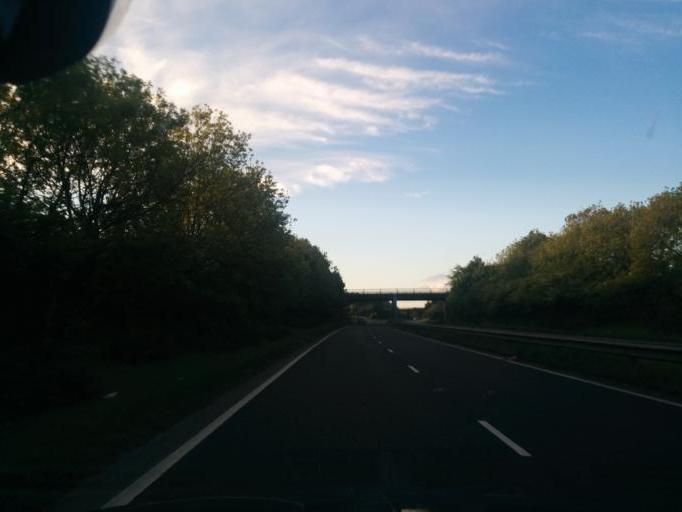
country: GB
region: England
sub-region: Northumberland
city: Cramlington
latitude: 55.1031
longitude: -1.5665
